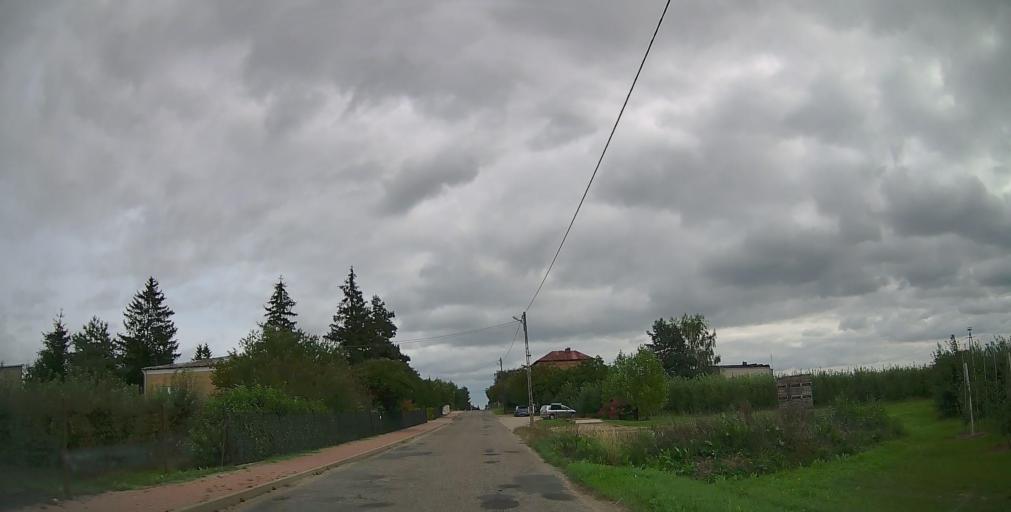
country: PL
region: Masovian Voivodeship
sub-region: Powiat grojecki
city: Belsk Duzy
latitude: 51.8185
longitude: 20.8231
